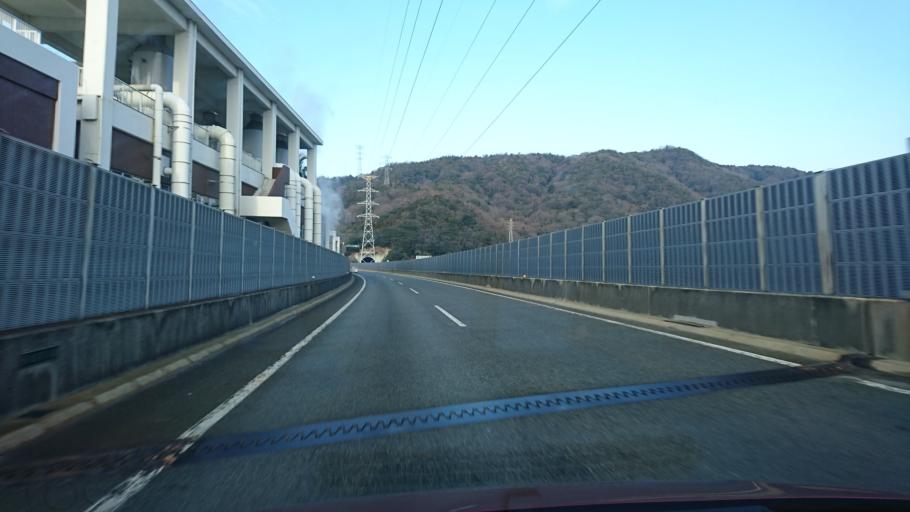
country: JP
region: Hyogo
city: Himeji
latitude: 34.8593
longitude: 134.7230
